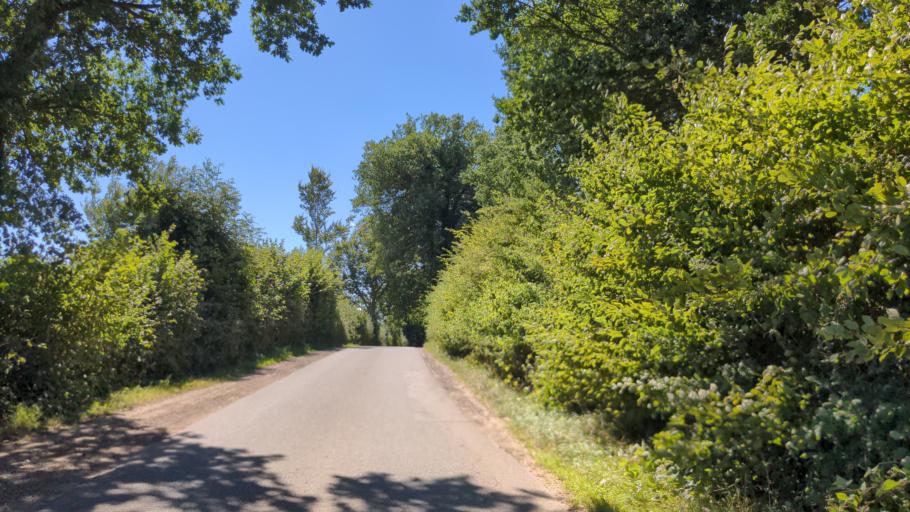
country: DE
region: Schleswig-Holstein
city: Altenkrempe
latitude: 54.1771
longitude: 10.8119
